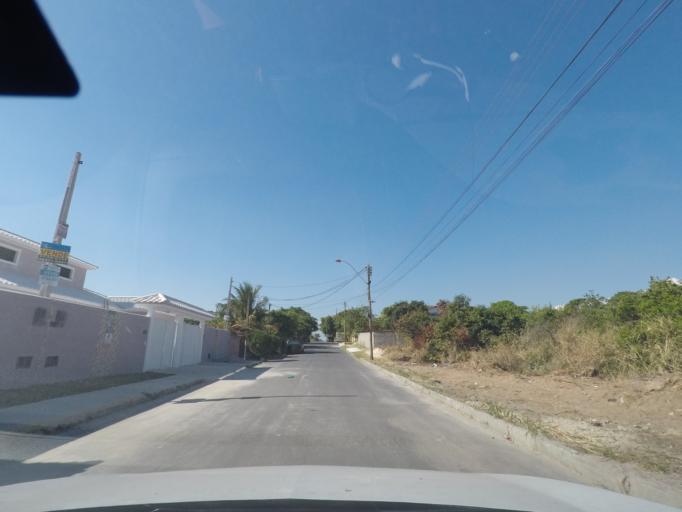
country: BR
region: Rio de Janeiro
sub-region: Marica
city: Marica
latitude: -22.9714
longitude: -42.9235
